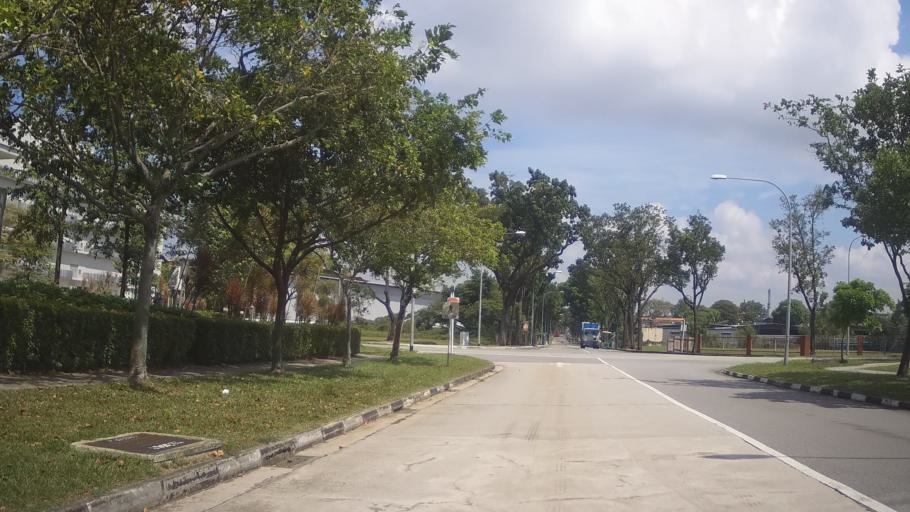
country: SG
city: Singapore
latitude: 1.3252
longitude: 103.7112
